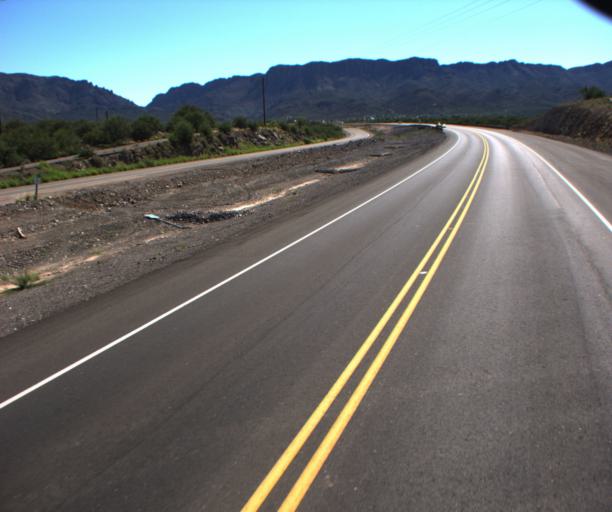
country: US
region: Arizona
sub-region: Pinal County
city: Superior
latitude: 33.2833
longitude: -111.1370
